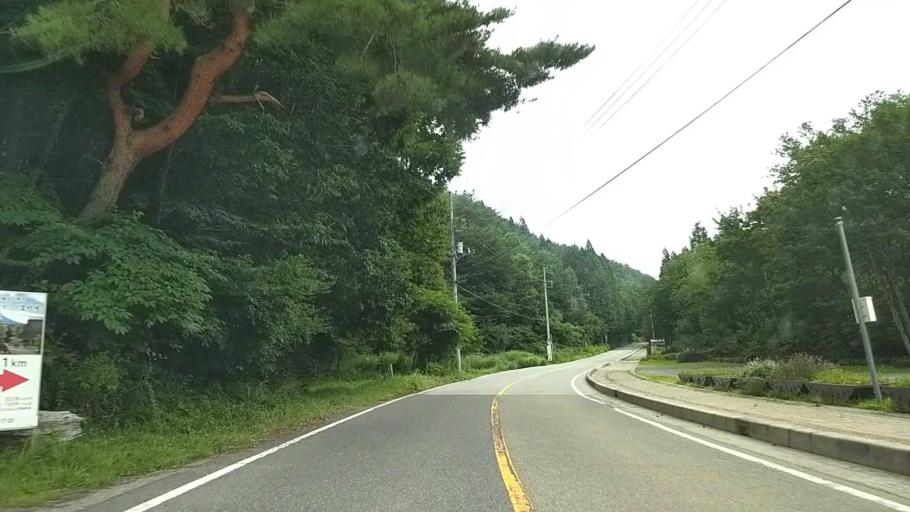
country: JP
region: Yamanashi
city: Fujikawaguchiko
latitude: 35.4987
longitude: 138.6524
